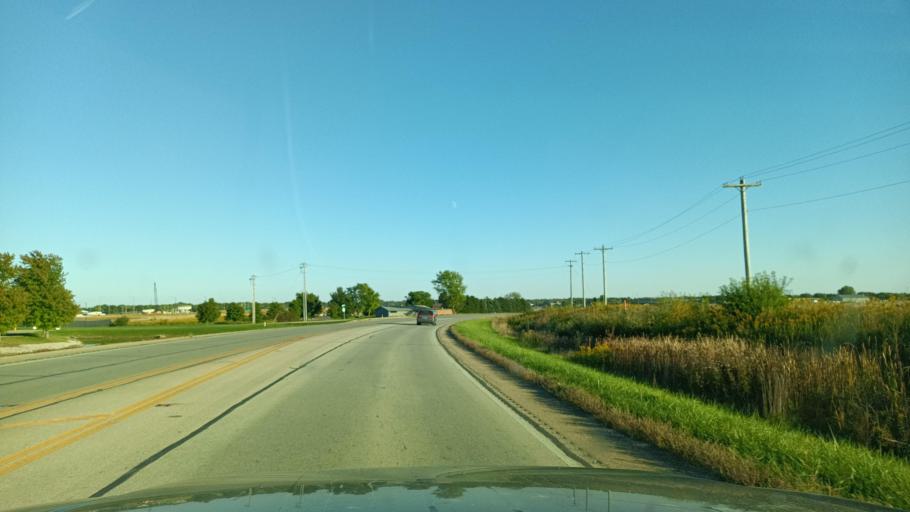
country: US
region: Illinois
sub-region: Champaign County
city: Champaign
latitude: 40.1496
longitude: -88.2929
